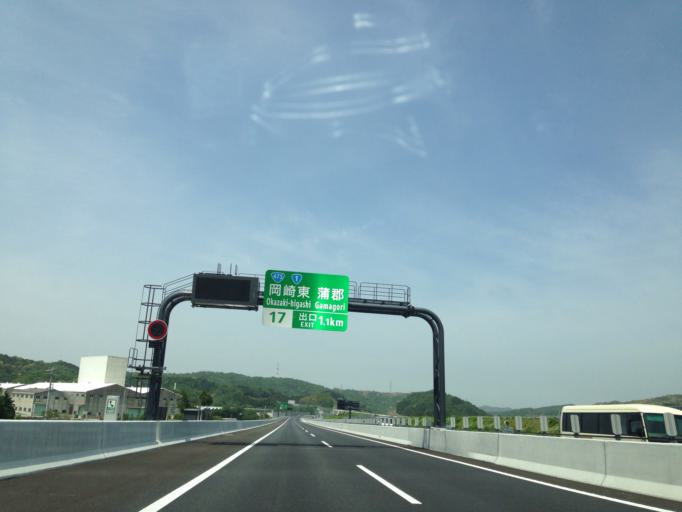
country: JP
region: Aichi
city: Gamagori
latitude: 34.9120
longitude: 137.2896
